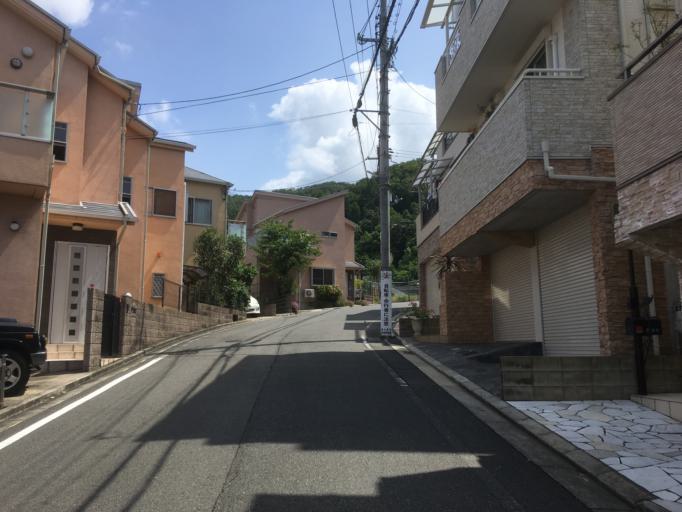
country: JP
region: Nara
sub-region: Ikoma-shi
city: Ikoma
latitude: 34.6874
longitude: 135.6566
